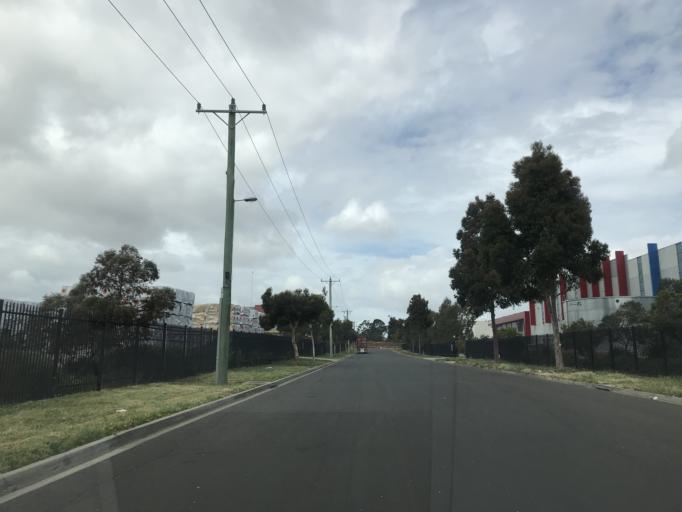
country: AU
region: Victoria
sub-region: Brimbank
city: Derrimut
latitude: -37.7892
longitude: 144.7752
